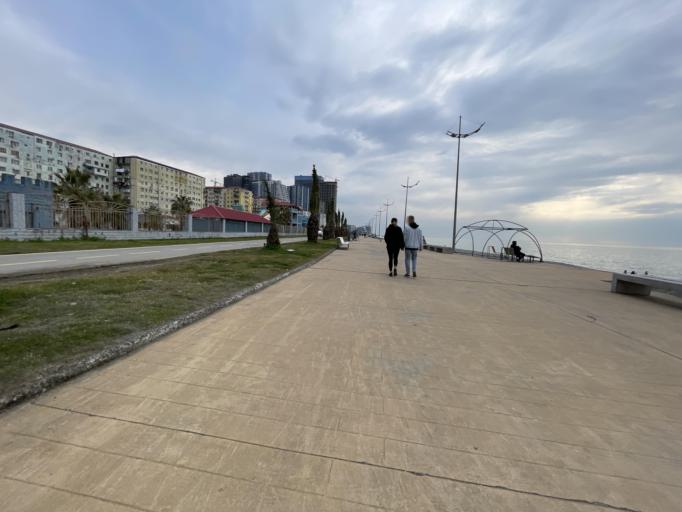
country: GE
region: Ajaria
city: Batumi
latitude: 41.6356
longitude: 41.6057
